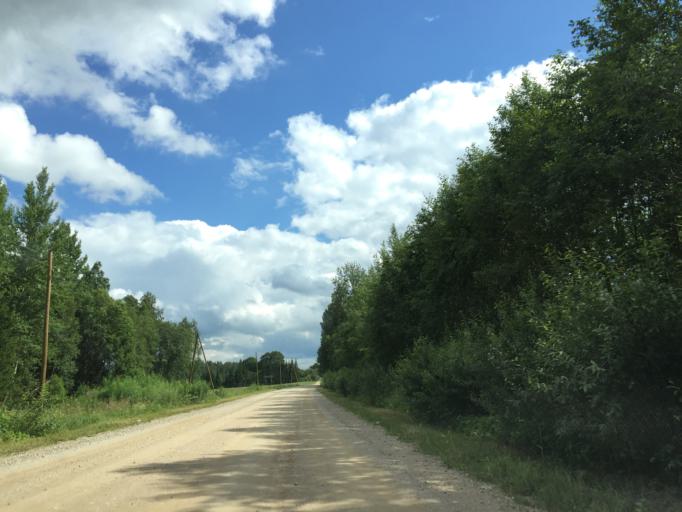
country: LV
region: Malpils
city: Malpils
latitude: 56.8748
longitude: 25.0022
